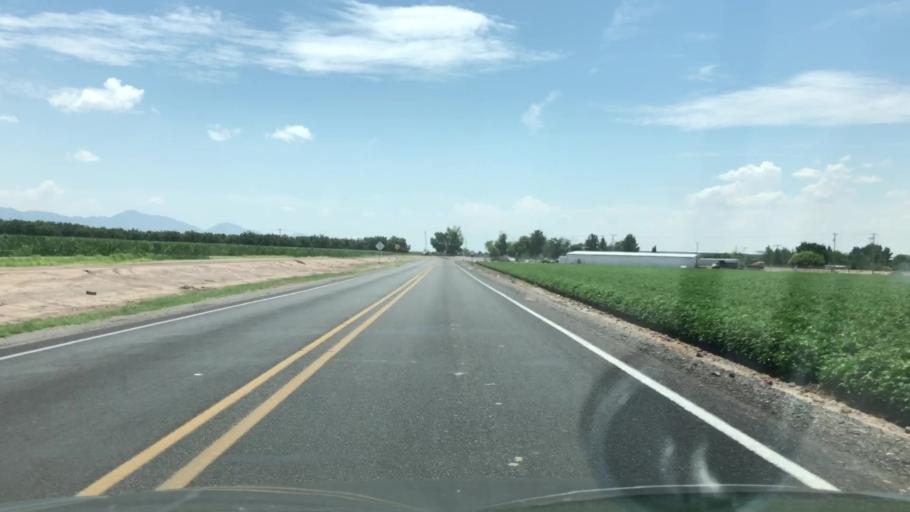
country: US
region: New Mexico
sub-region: Dona Ana County
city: Vado
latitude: 32.0646
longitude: -106.6788
